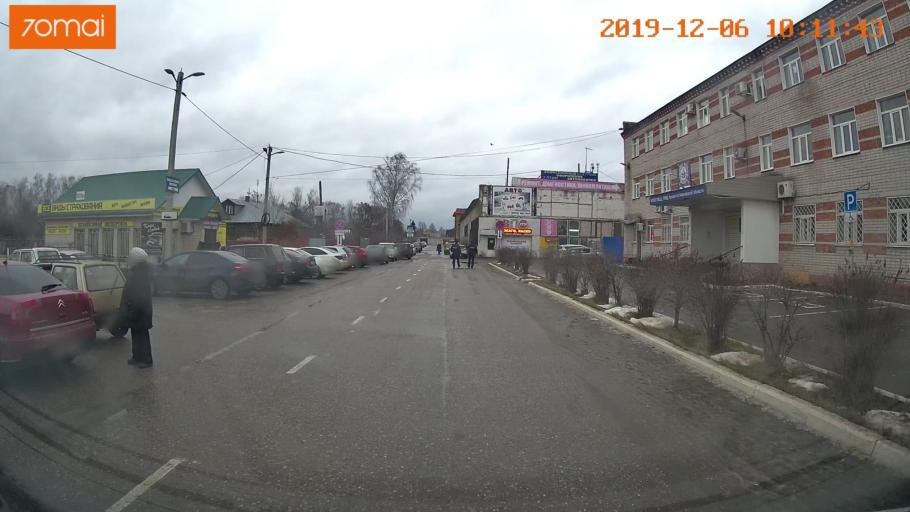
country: RU
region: Ivanovo
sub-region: Gorod Ivanovo
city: Ivanovo
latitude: 57.0315
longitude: 40.9747
